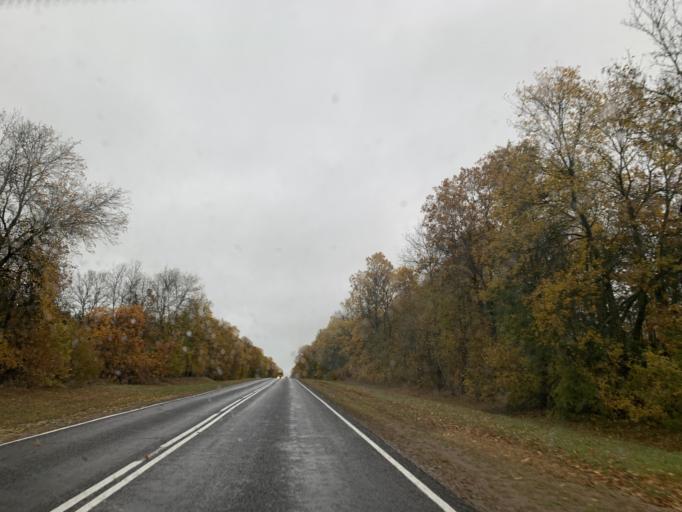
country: BY
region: Minsk
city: Novy Svyerzhan'
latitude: 53.4343
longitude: 26.6479
